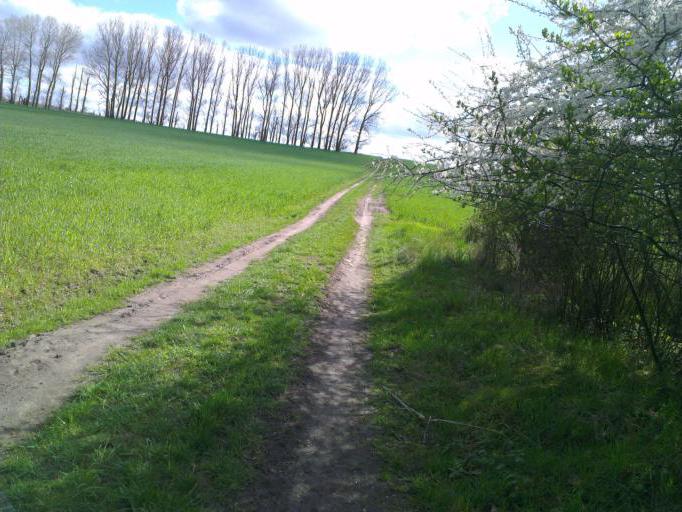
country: DK
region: Capital Region
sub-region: Frederikssund Kommune
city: Jaegerspris
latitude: 55.8108
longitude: 12.0025
